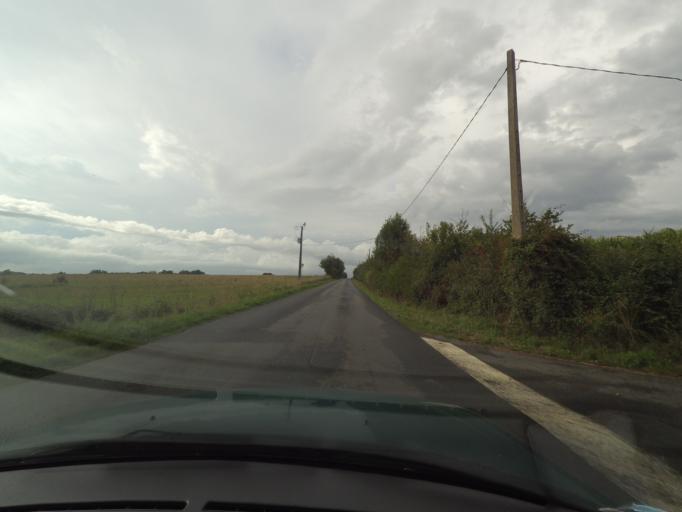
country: FR
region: Limousin
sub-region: Departement de la Haute-Vienne
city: Nexon
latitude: 45.7156
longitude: 1.1574
